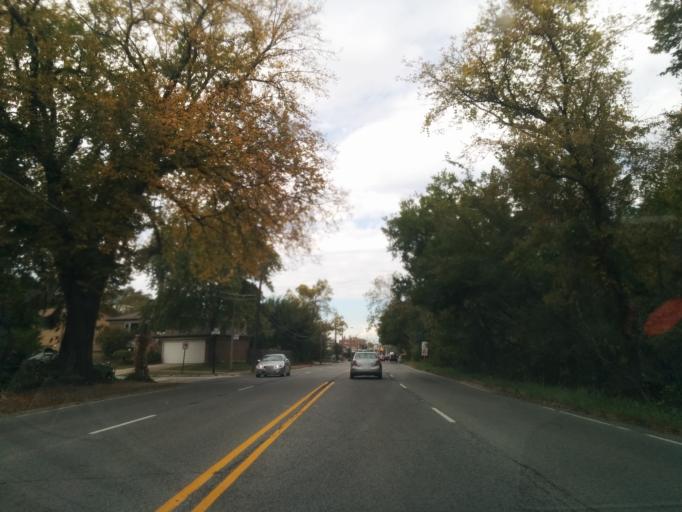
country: US
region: Illinois
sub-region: Cook County
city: River Grove
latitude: 41.9267
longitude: -87.8445
